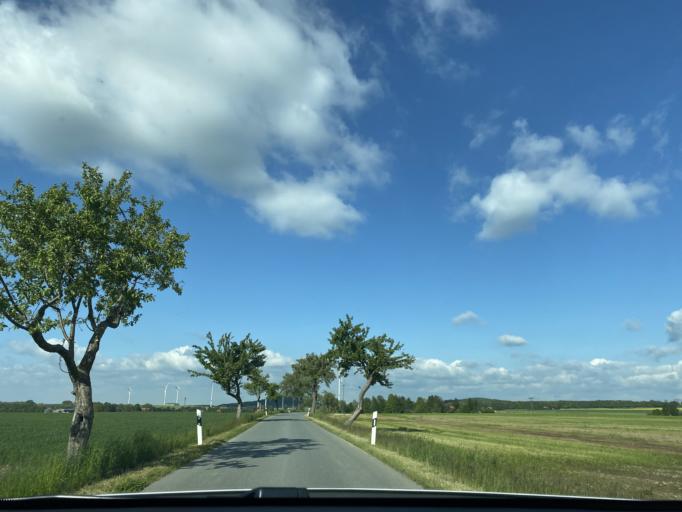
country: DE
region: Saxony
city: Sohland am Rotstein
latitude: 51.0818
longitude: 14.7841
